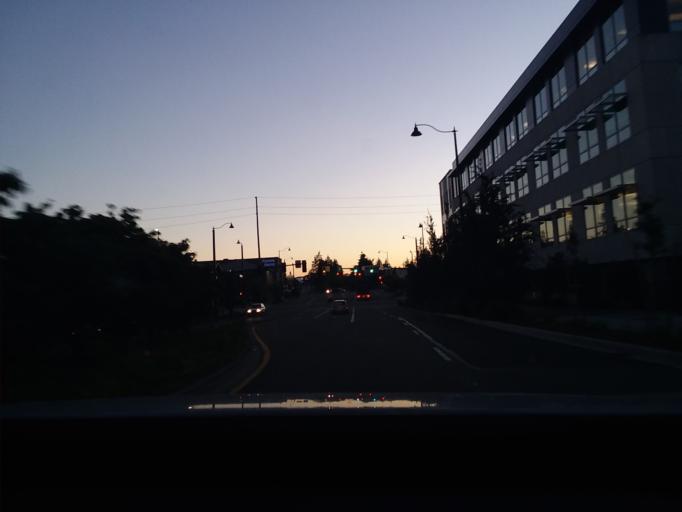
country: US
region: Washington
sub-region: King County
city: Shoreline
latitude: 47.7560
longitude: -122.3430
